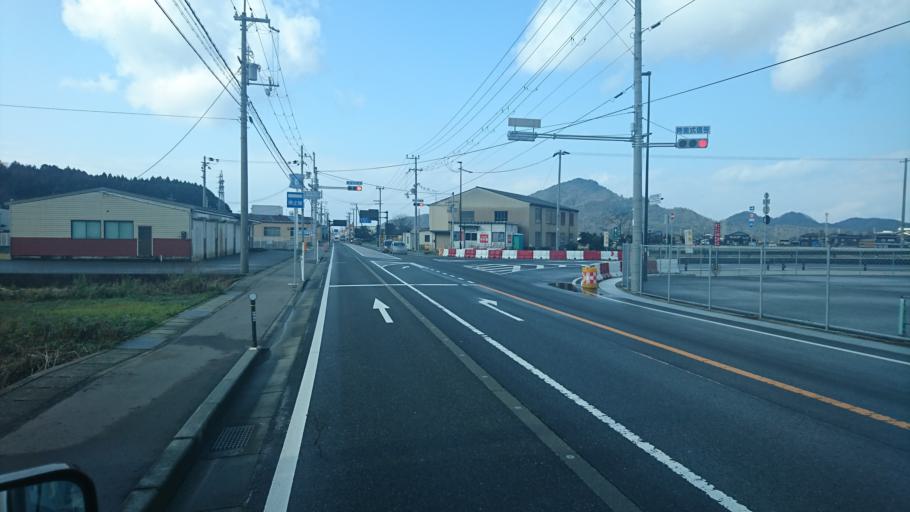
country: JP
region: Tottori
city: Tottori
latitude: 35.6110
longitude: 134.4698
